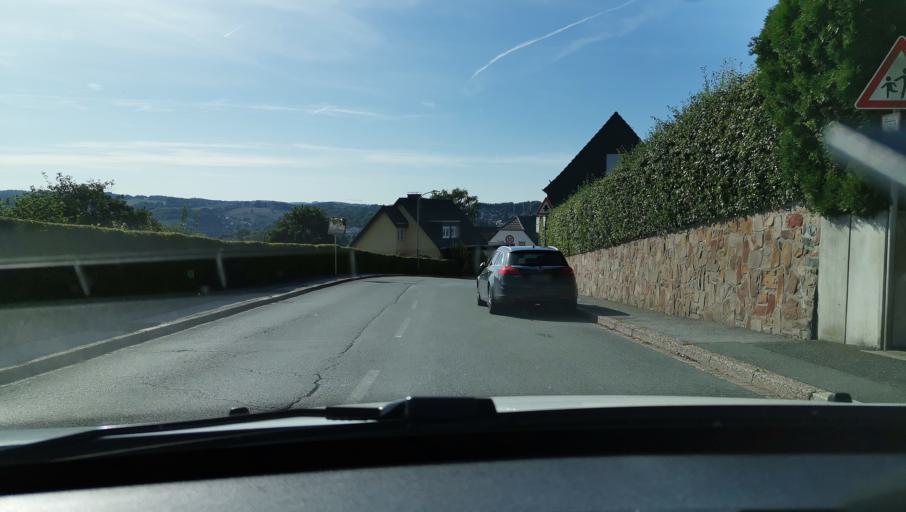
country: DE
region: North Rhine-Westphalia
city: Ennepetal
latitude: 51.3131
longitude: 7.3869
